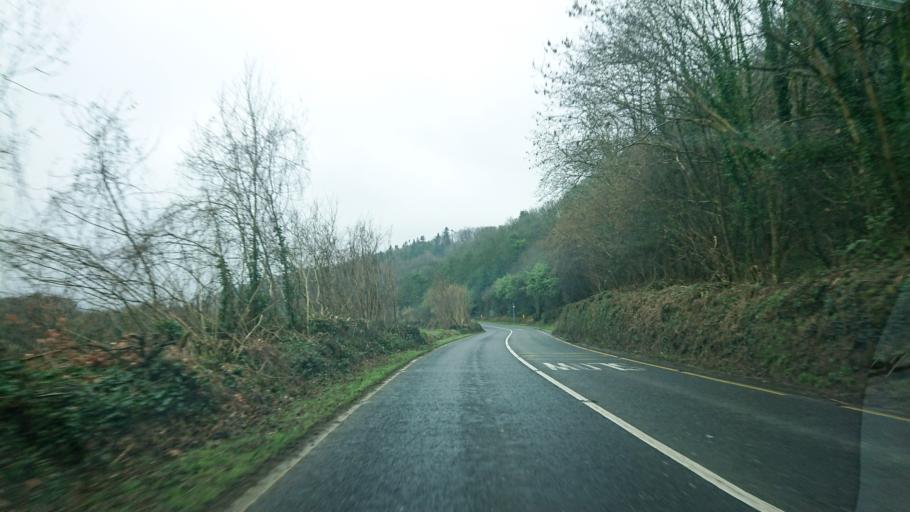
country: IE
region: Munster
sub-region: County Cork
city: Bandon
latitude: 51.7666
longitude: -8.6707
